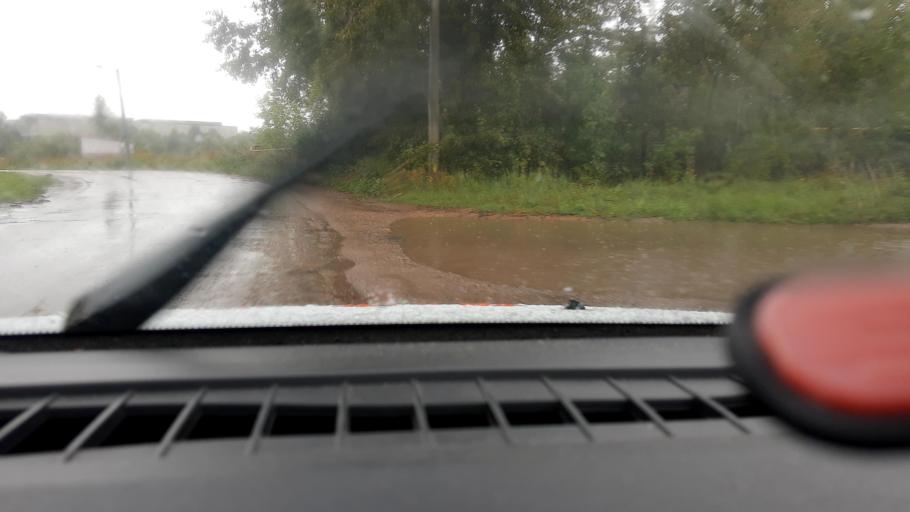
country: RU
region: Nizjnij Novgorod
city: Lyskovo
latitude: 56.0280
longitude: 45.0292
